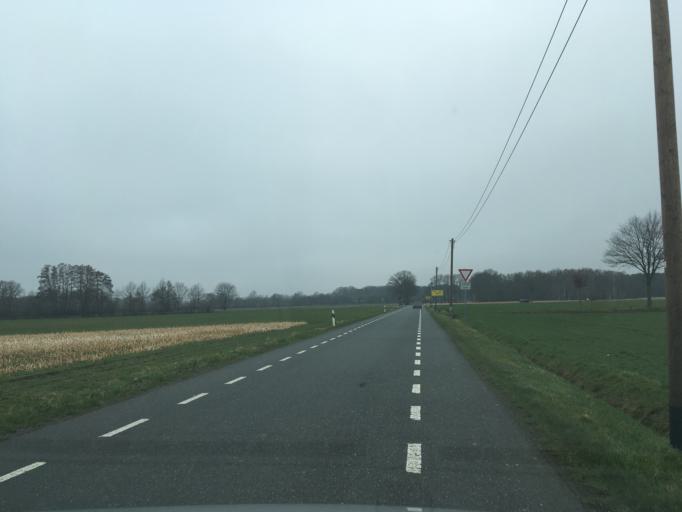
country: DE
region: North Rhine-Westphalia
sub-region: Regierungsbezirk Munster
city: Rhede
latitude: 51.8862
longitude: 6.6877
